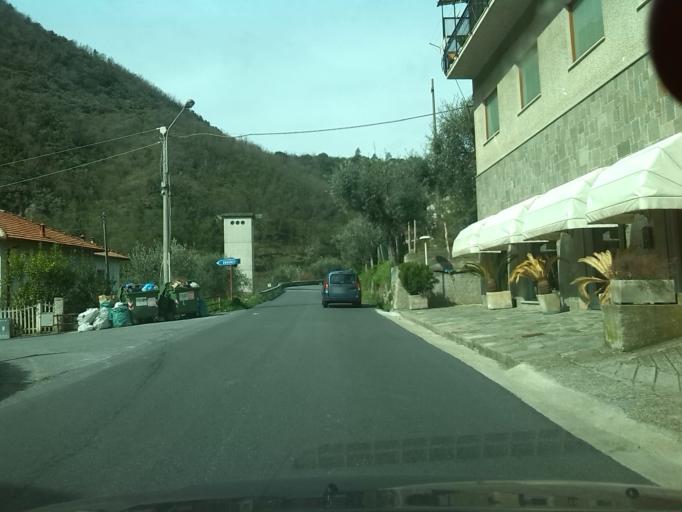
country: IT
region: Liguria
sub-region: Provincia di Imperia
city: Borgo di Ranzo
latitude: 44.0589
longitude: 8.0026
